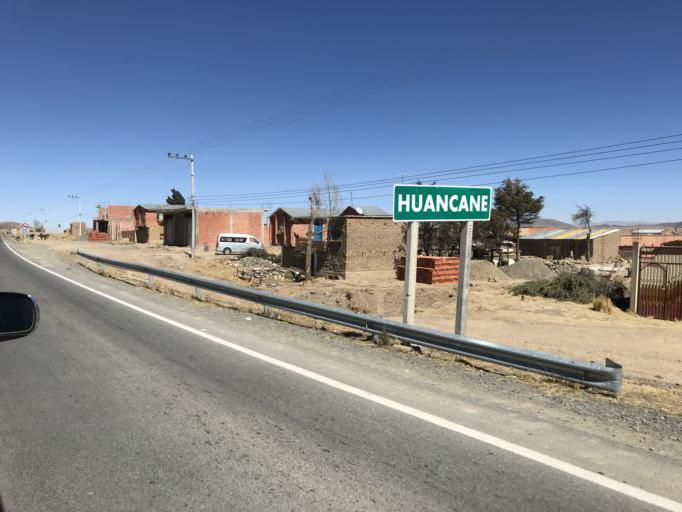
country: BO
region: La Paz
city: Batallas
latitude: -16.2585
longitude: -68.5620
